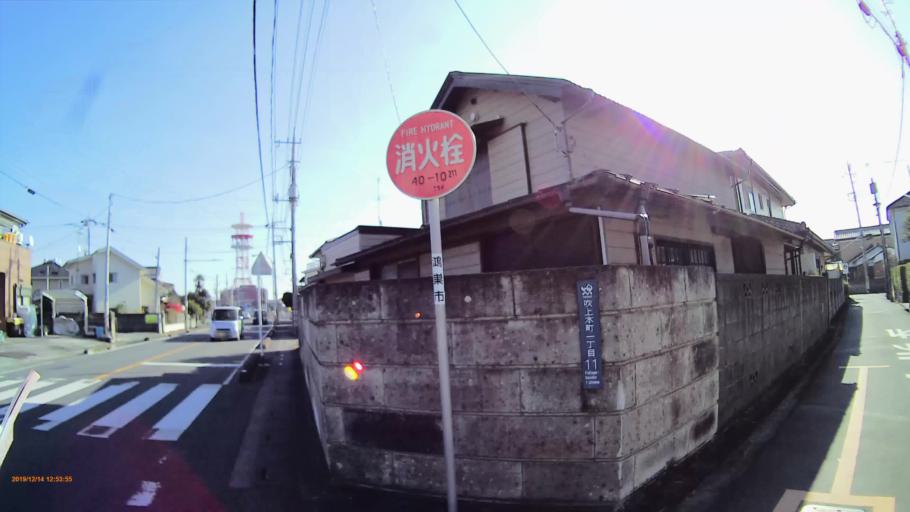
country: JP
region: Saitama
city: Fukiage-fujimi
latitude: 36.1031
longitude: 139.4566
